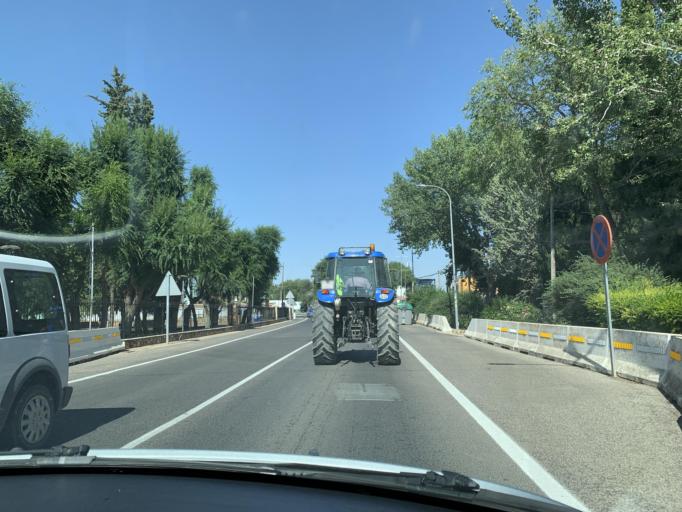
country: ES
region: Castille-La Mancha
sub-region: Provincia de Ciudad Real
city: Argamasilla de Alba
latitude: 39.1298
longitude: -3.0834
